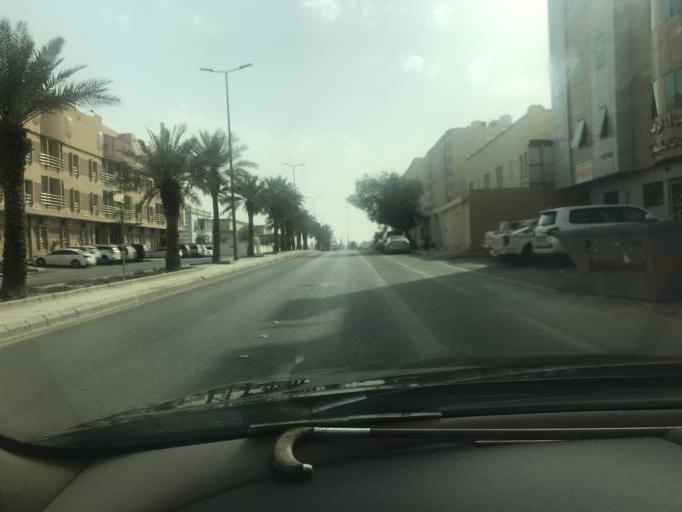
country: SA
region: Ar Riyad
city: Riyadh
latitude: 24.7331
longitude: 46.7562
